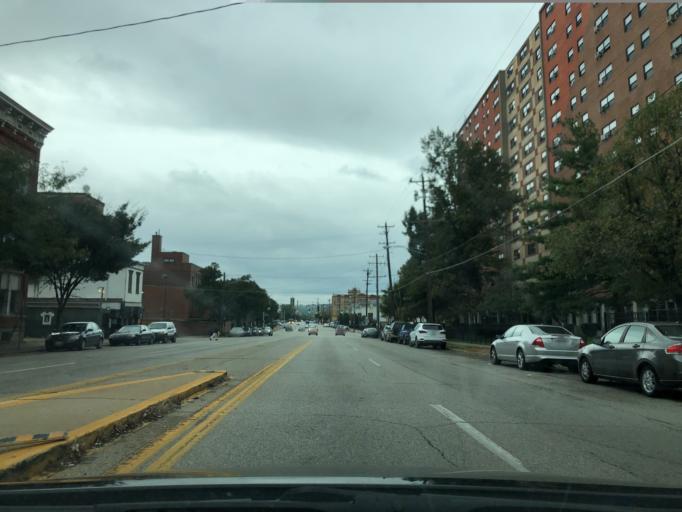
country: US
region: Kentucky
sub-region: Kenton County
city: Ludlow
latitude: 39.1150
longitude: -84.5274
